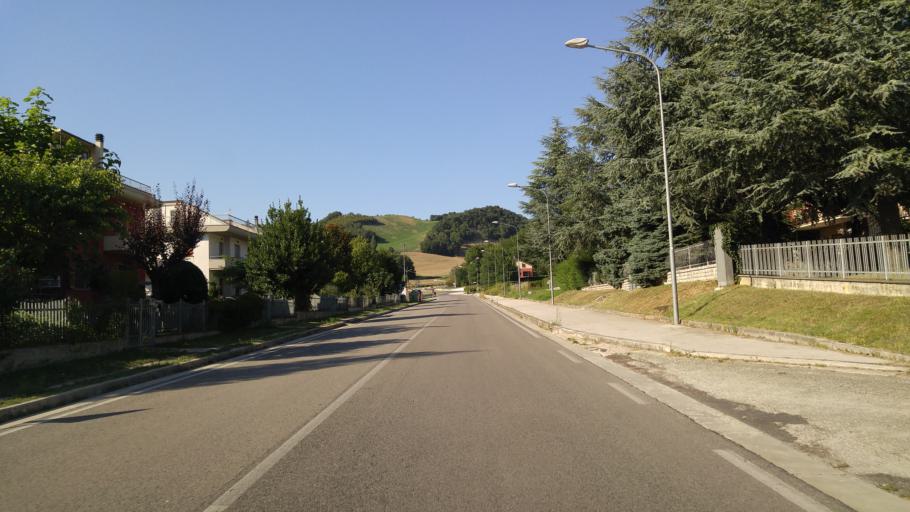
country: IT
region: The Marches
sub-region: Provincia di Pesaro e Urbino
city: Urbania
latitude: 43.6732
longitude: 12.5235
